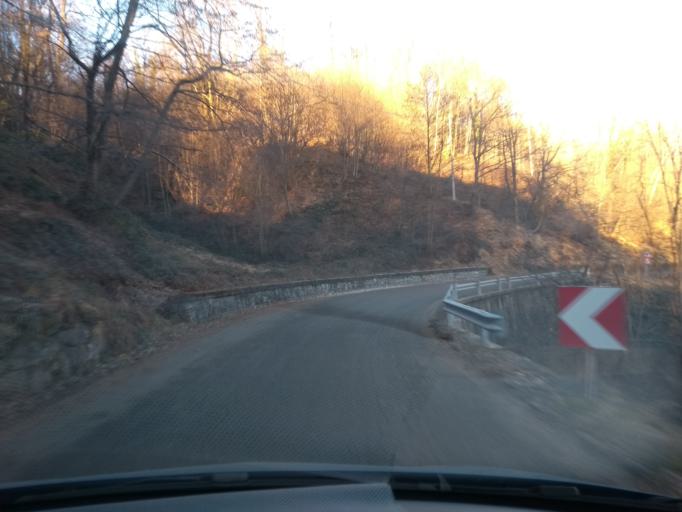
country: IT
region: Piedmont
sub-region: Provincia di Torino
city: Corio
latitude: 45.3204
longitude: 7.5272
